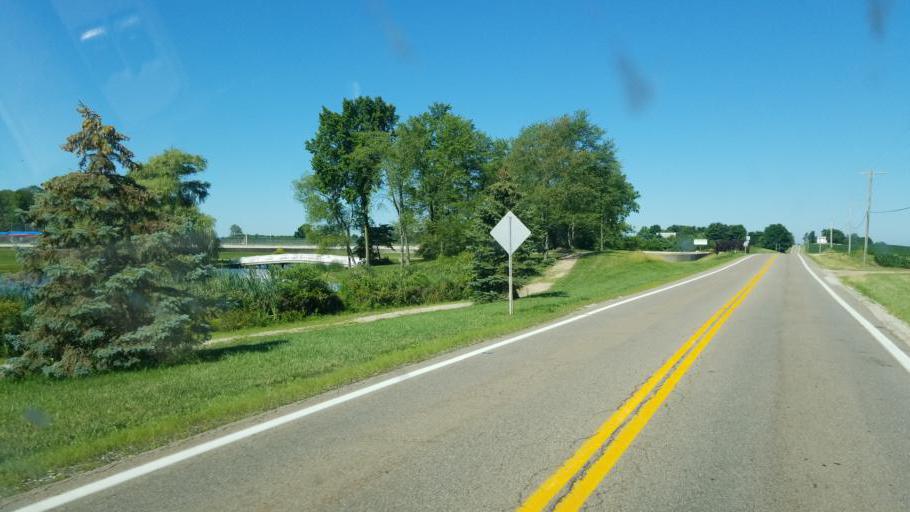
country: US
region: Ohio
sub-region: Knox County
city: Centerburg
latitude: 40.3989
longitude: -82.7100
